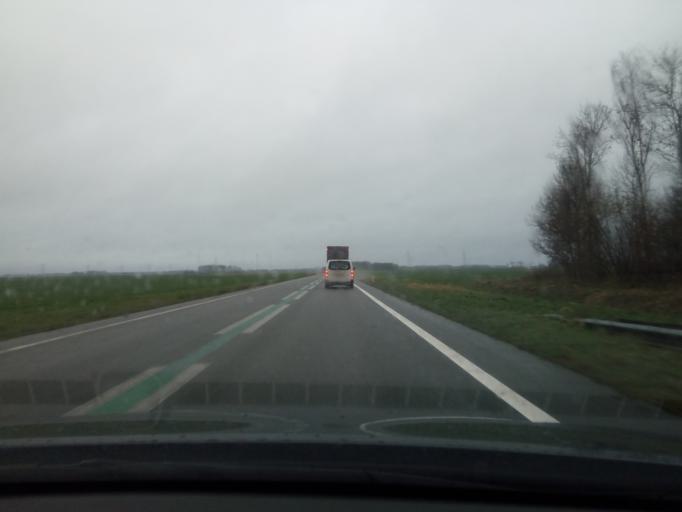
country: NL
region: Groningen
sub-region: Gemeente Slochteren
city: Slochteren
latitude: 53.2041
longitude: 6.8873
